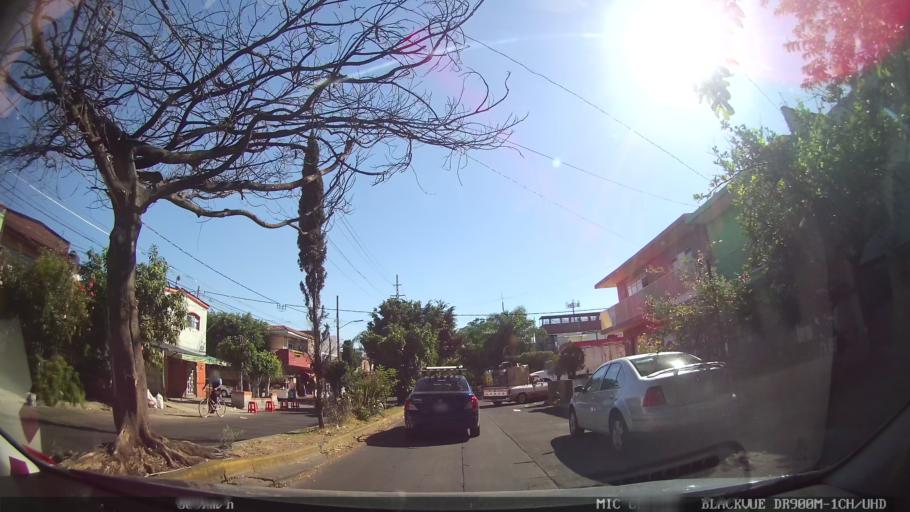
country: MX
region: Jalisco
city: Tlaquepaque
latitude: 20.6677
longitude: -103.2847
